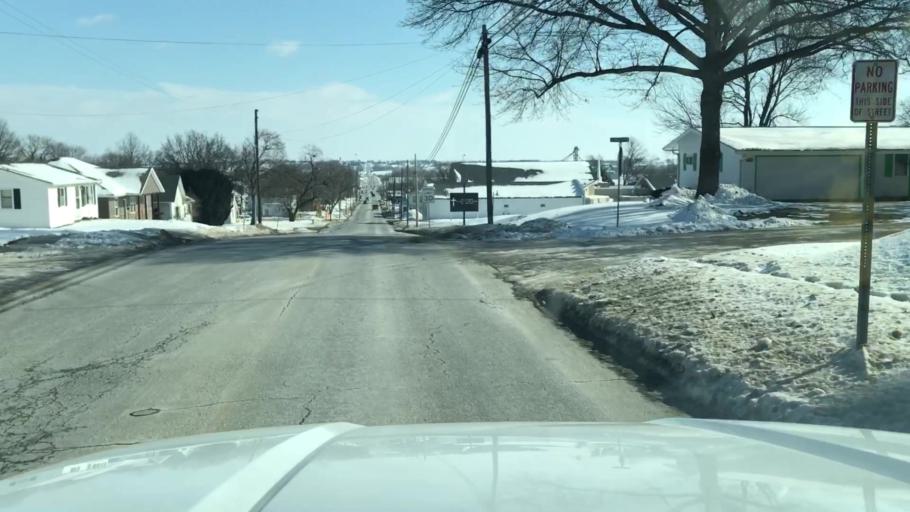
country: US
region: Missouri
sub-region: Nodaway County
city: Maryville
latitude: 40.3455
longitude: -94.8625
